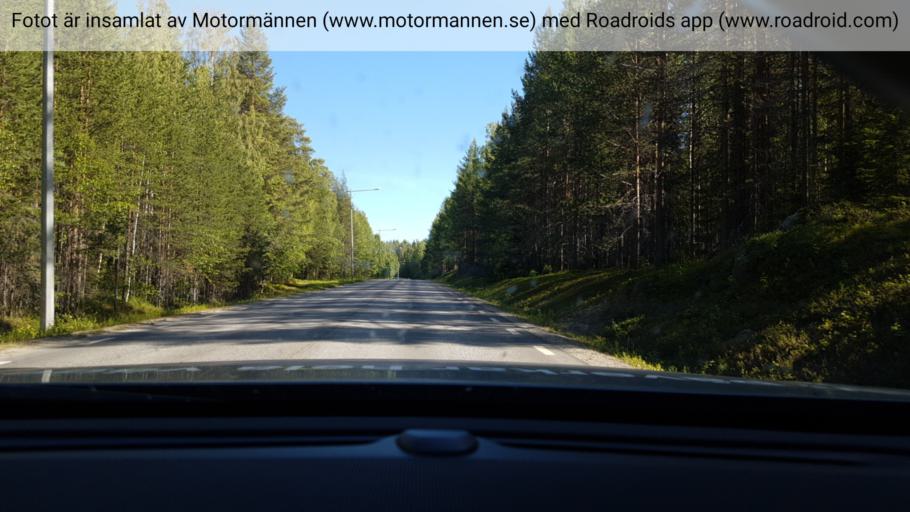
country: SE
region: Vaesterbotten
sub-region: Lycksele Kommun
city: Lycksele
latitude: 64.6127
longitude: 18.6432
